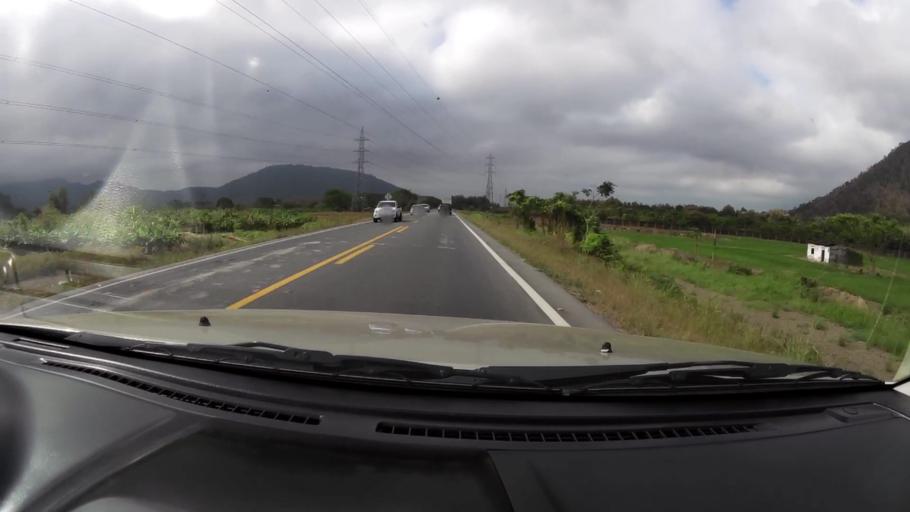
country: EC
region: Guayas
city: Naranjal
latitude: -2.4120
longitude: -79.6239
